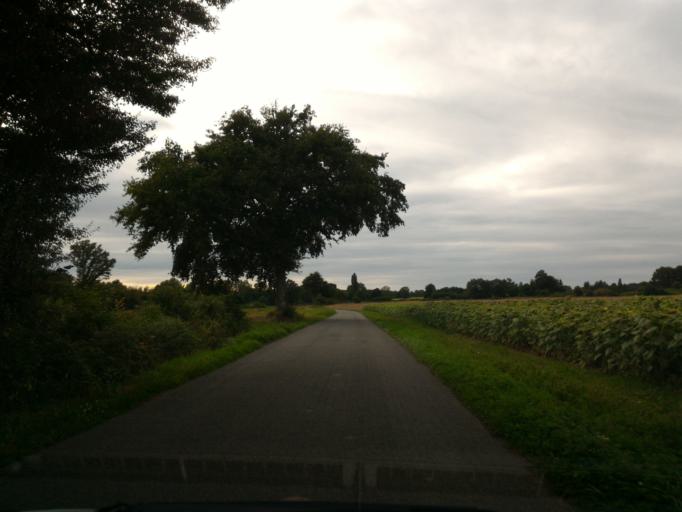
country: FR
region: Poitou-Charentes
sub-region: Departement de la Charente
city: Brigueuil
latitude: 45.9266
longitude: 0.8332
